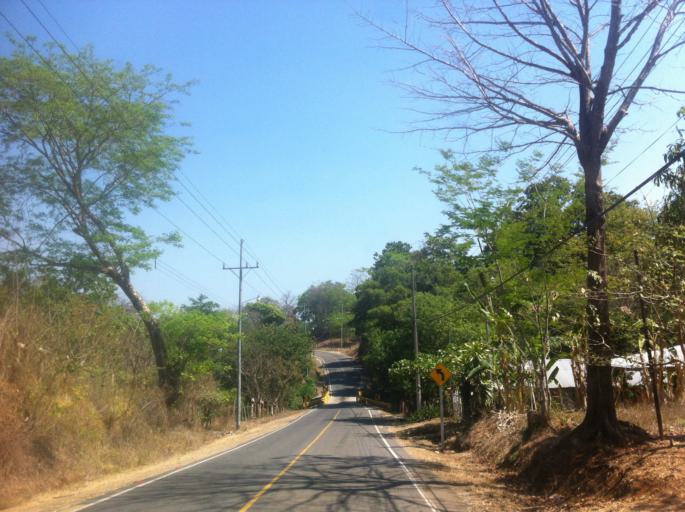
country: CR
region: Guanacaste
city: Hojancha
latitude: 10.0189
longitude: -85.5022
